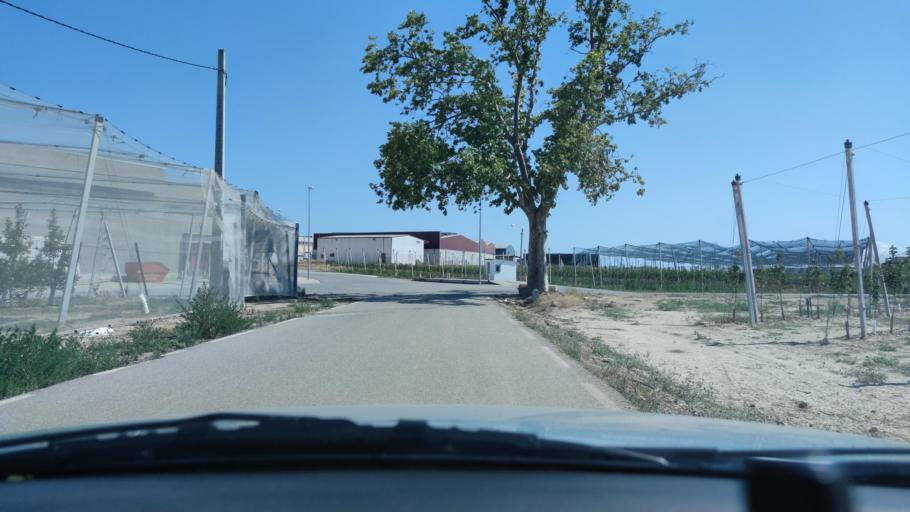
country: ES
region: Catalonia
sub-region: Provincia de Lleida
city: Torrefarrera
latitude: 41.6806
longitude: 0.6279
